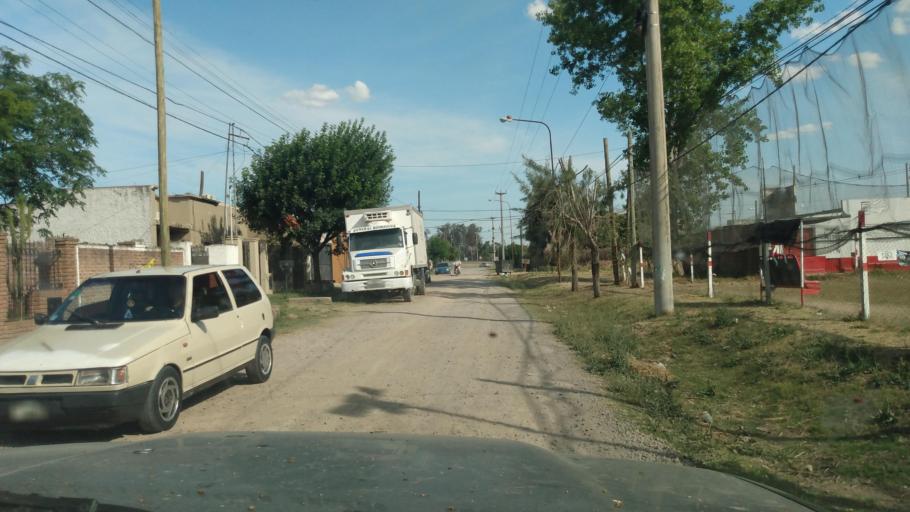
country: AR
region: Buenos Aires
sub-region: Partido de Lujan
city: Lujan
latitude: -34.5526
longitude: -59.1041
